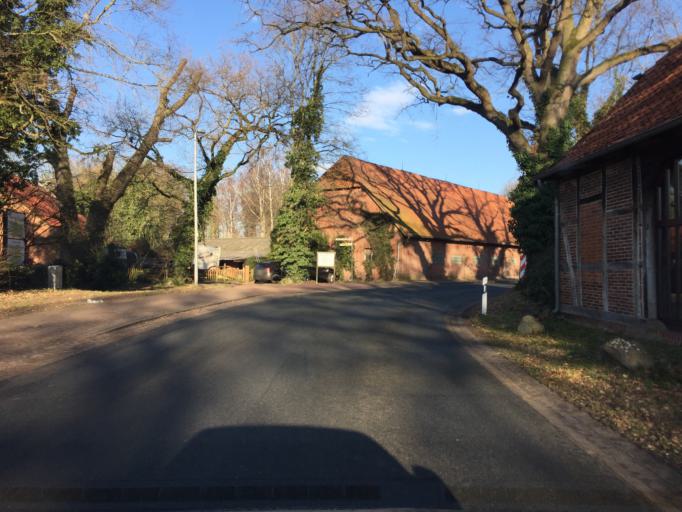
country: DE
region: Lower Saxony
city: Husum
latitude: 52.5503
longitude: 9.2112
